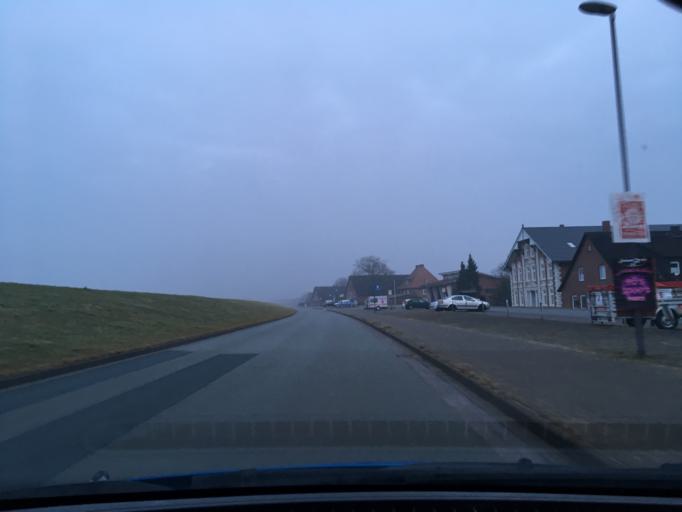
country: DE
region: Lower Saxony
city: Stelle
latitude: 53.3999
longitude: 10.1592
